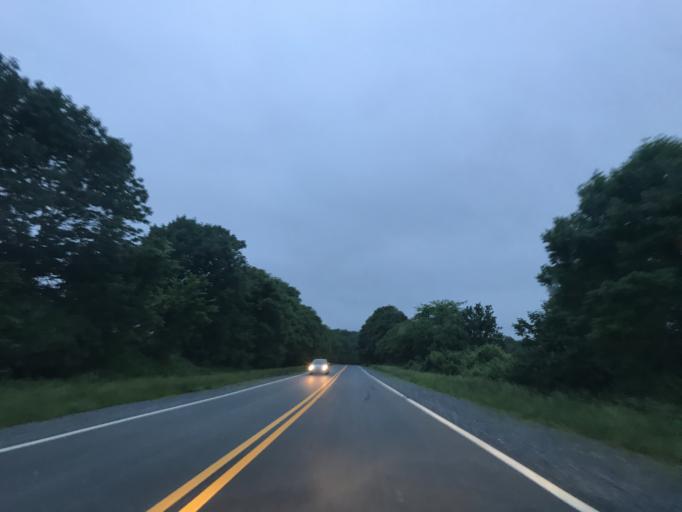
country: US
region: Maryland
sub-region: Frederick County
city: Linganore
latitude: 39.3795
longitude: -77.2560
